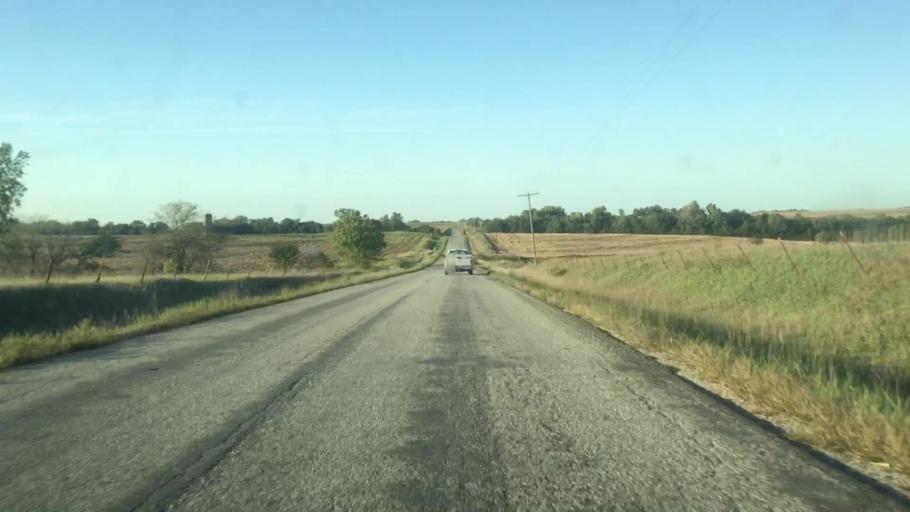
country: US
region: Kansas
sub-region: Brown County
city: Horton
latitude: 39.5537
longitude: -95.4021
